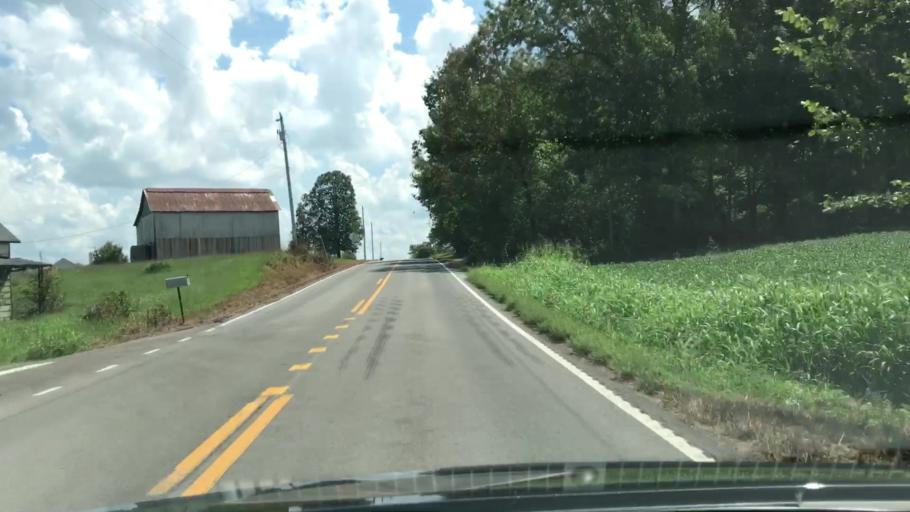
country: US
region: Tennessee
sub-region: Robertson County
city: Springfield
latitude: 36.5970
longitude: -86.9098
